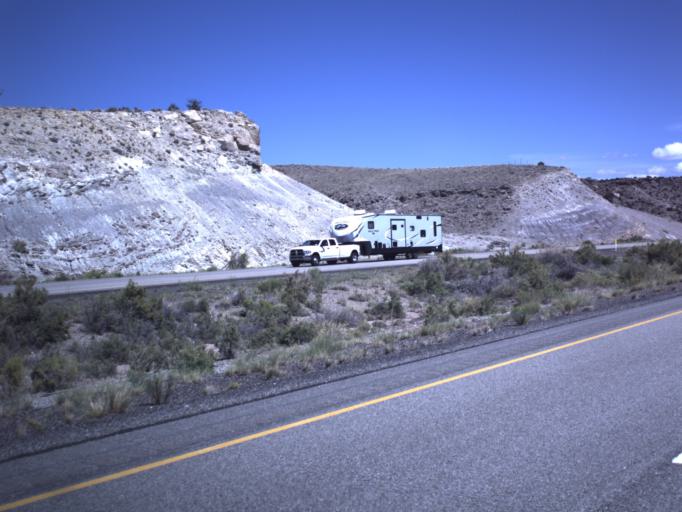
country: US
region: Utah
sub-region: Emery County
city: Ferron
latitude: 38.8170
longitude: -111.1733
